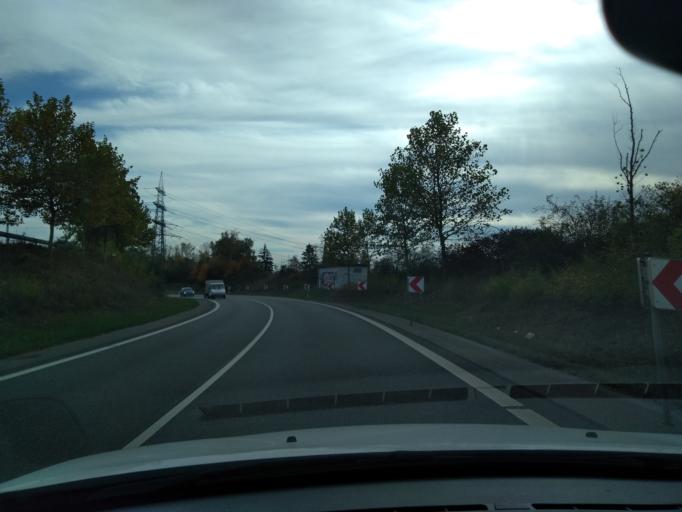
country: DE
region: Saarland
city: Ensdorf
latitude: 49.2948
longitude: 6.7744
